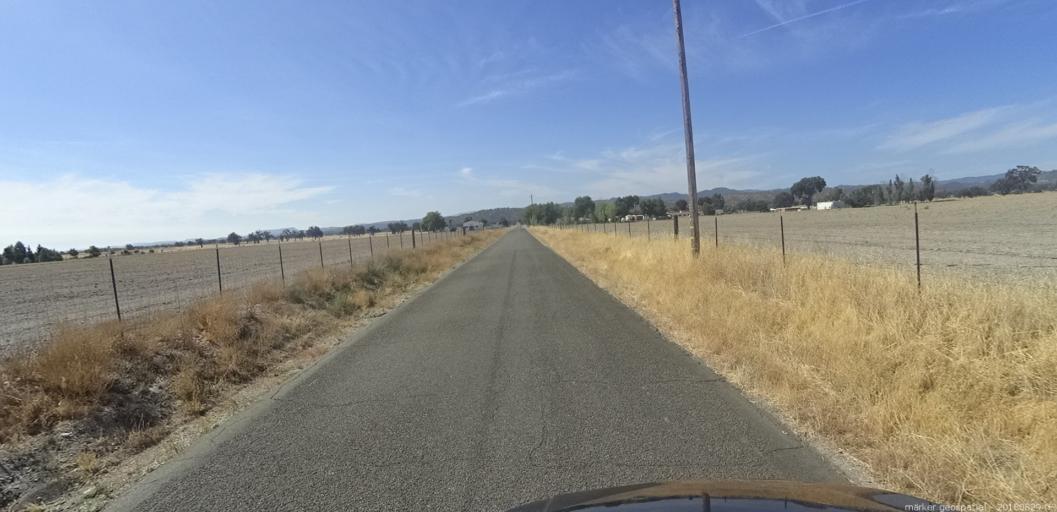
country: US
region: California
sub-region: Monterey County
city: King City
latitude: 35.9465
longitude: -121.0821
